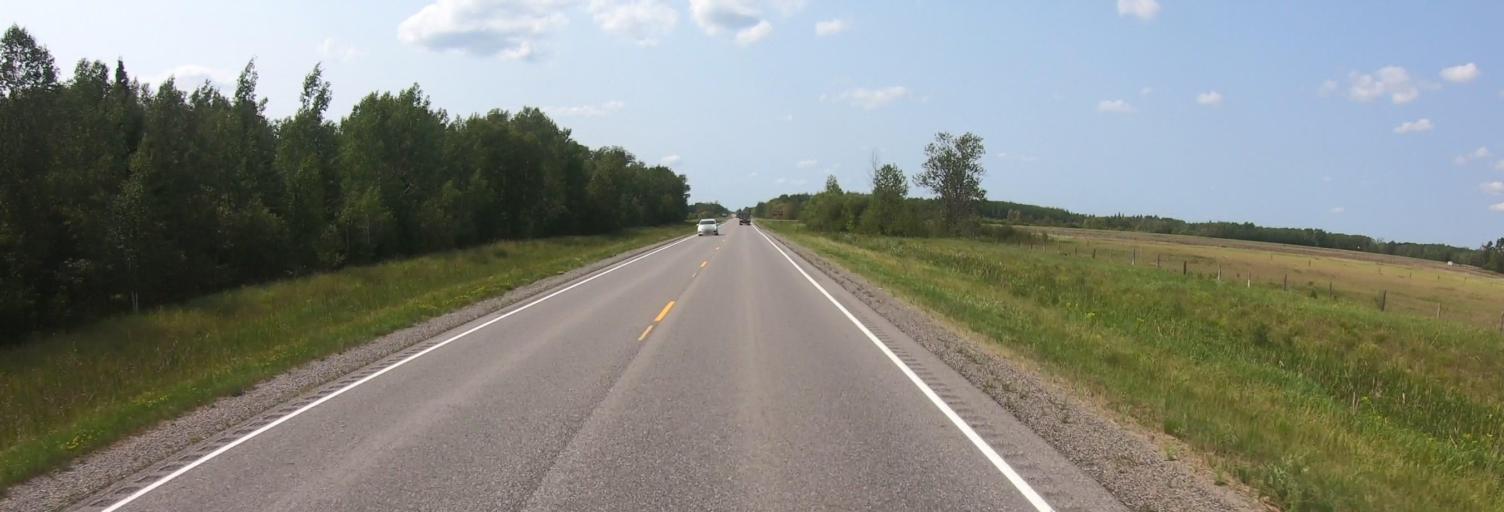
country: US
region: Minnesota
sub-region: Lake of the Woods County
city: Baudette
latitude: 48.6278
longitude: -94.0539
